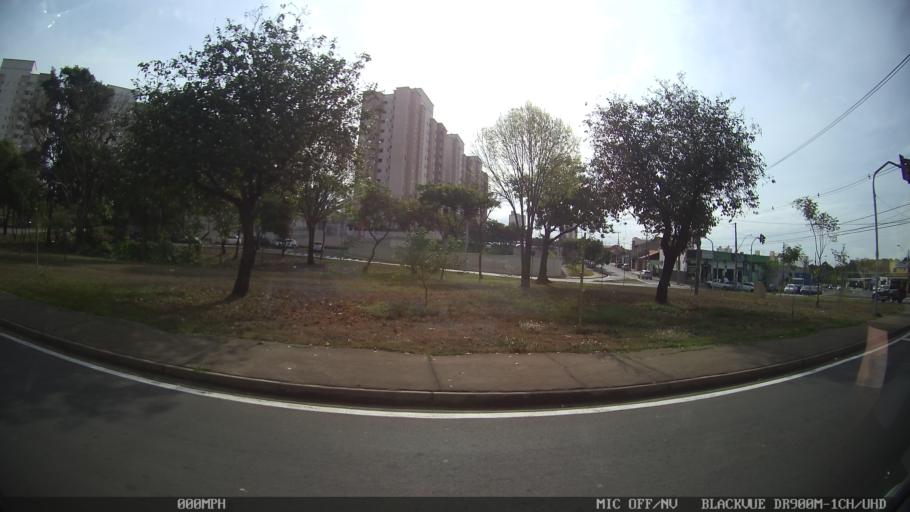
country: BR
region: Sao Paulo
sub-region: Piracicaba
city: Piracicaba
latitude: -22.7444
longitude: -47.6310
